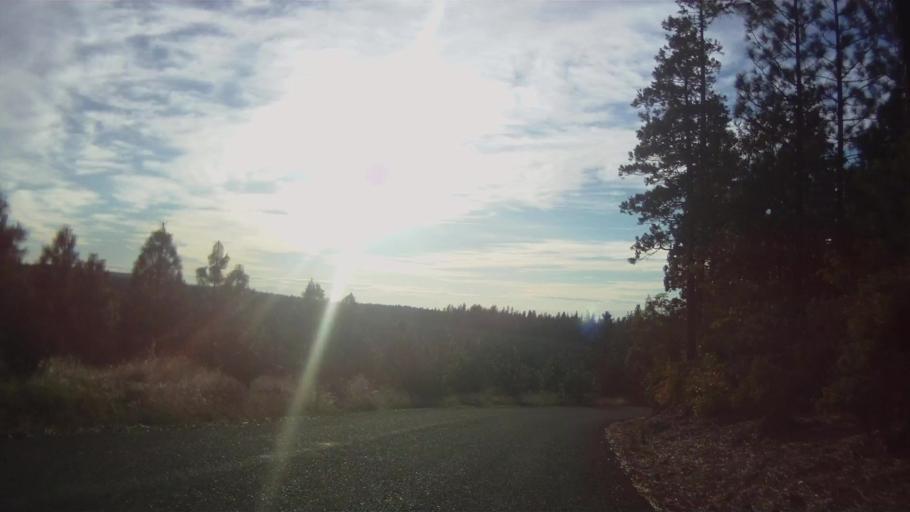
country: US
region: California
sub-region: Shasta County
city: Shingletown
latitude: 40.6336
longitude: -121.8538
